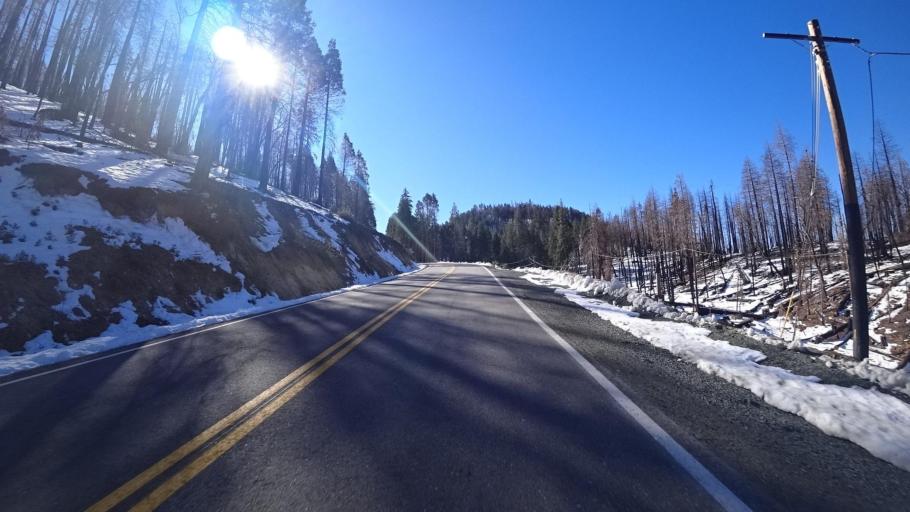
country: US
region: California
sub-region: Kern County
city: Alta Sierra
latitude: 35.7434
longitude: -118.5568
